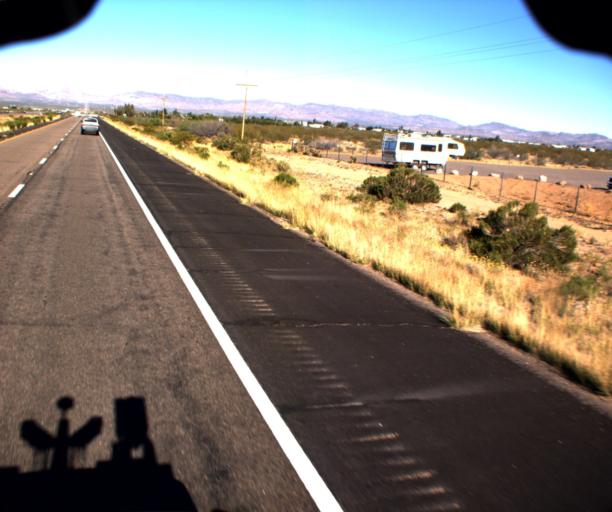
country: US
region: Arizona
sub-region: Mohave County
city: Golden Valley
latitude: 35.2233
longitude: -114.2397
